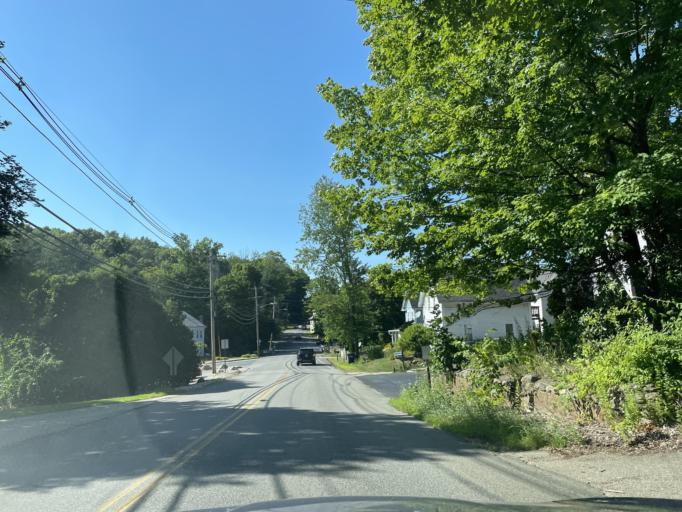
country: US
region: Massachusetts
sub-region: Worcester County
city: Charlton
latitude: 42.1475
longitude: -71.9884
